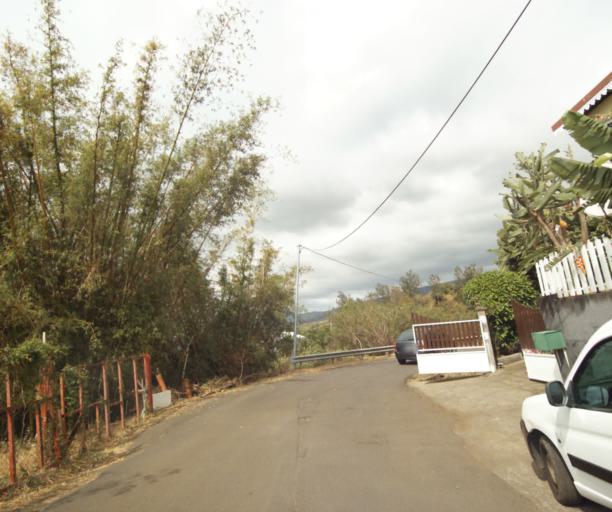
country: RE
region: Reunion
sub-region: Reunion
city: Saint-Paul
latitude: -21.0316
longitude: 55.2945
